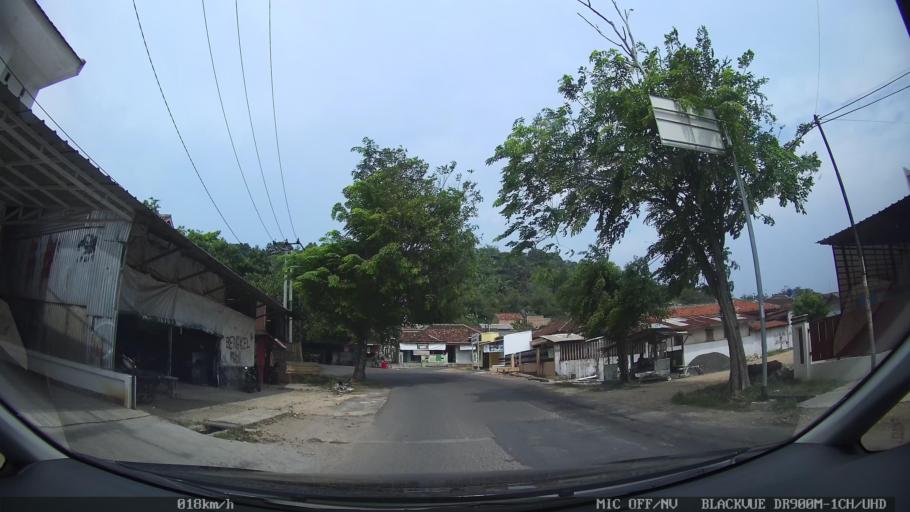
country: ID
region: Lampung
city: Bandarlampung
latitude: -5.4305
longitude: 105.2774
